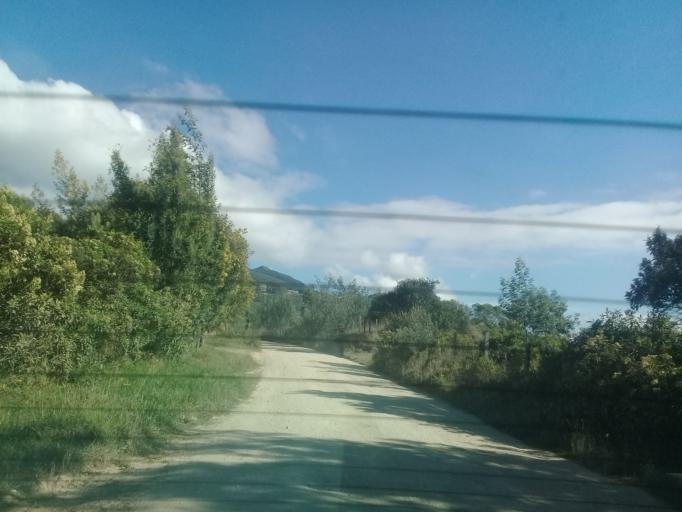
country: CO
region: Cundinamarca
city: Tocancipa
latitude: 4.9285
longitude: -73.8813
